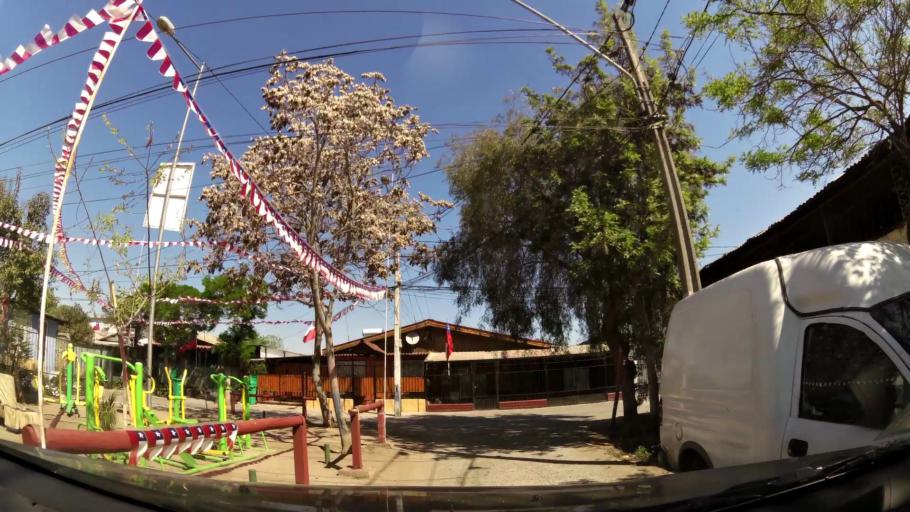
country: CL
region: Santiago Metropolitan
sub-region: Provincia de Maipo
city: San Bernardo
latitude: -33.5801
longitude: -70.7036
